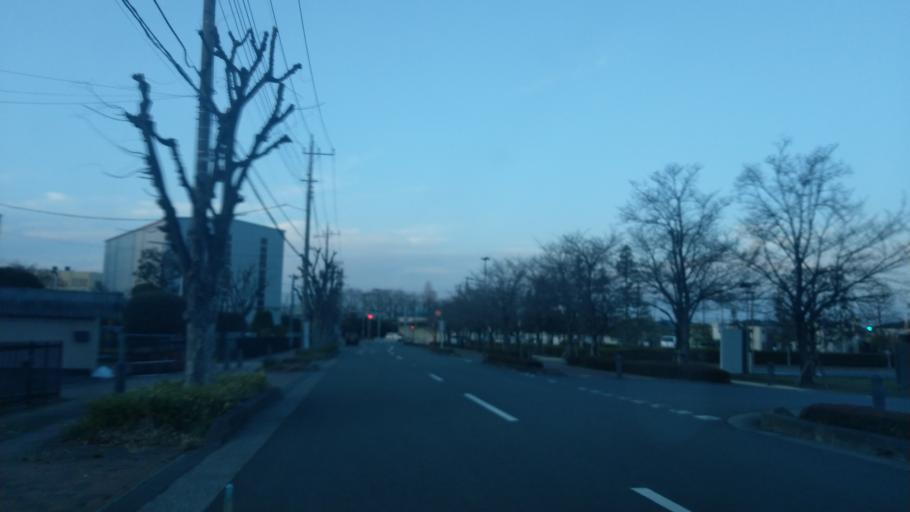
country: JP
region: Saitama
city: Shiki
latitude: 35.8569
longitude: 139.6083
